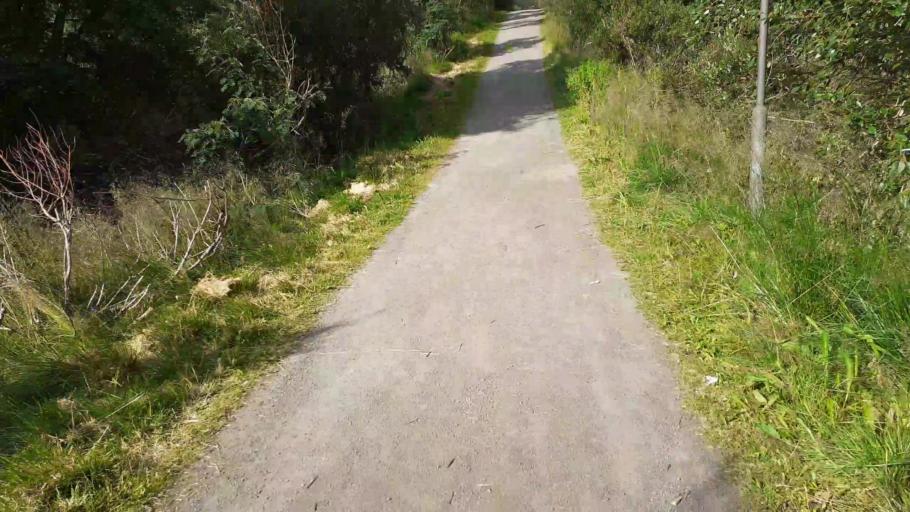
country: IS
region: Northeast
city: Akureyri
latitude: 65.6434
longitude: -18.0862
